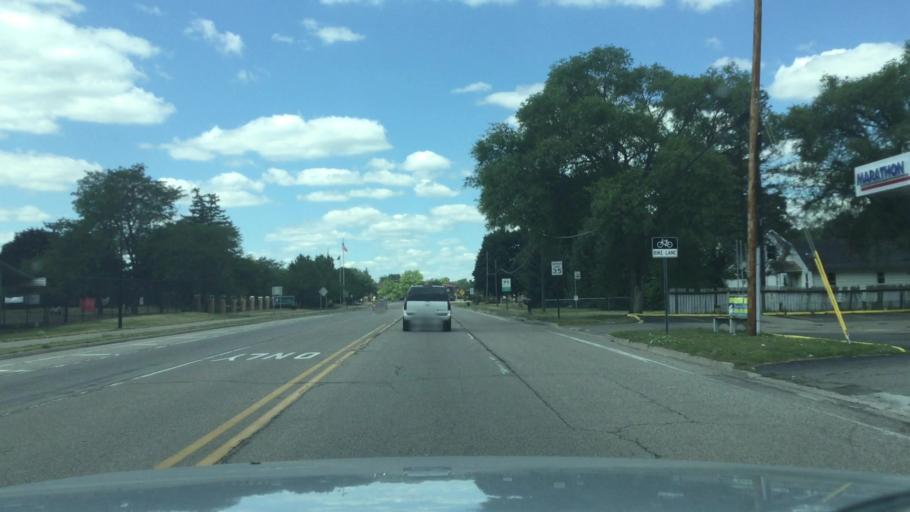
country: US
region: Michigan
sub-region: Washtenaw County
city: Ypsilanti
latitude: 42.2150
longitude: -83.5628
